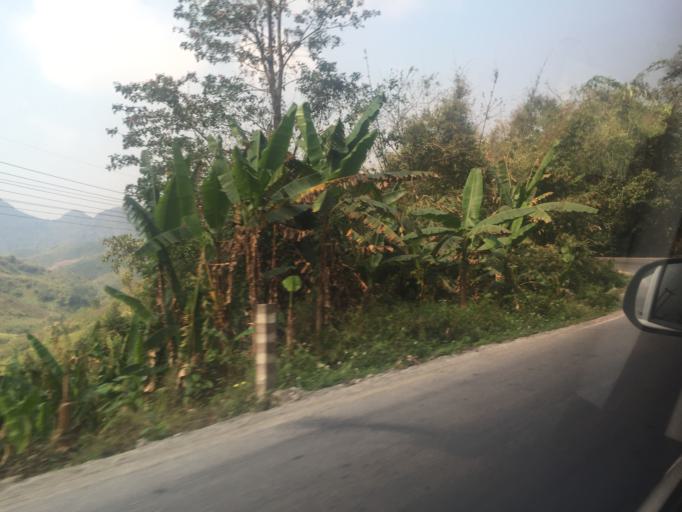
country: LA
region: Oudomxai
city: Muang Xay
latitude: 20.8536
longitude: 101.8131
